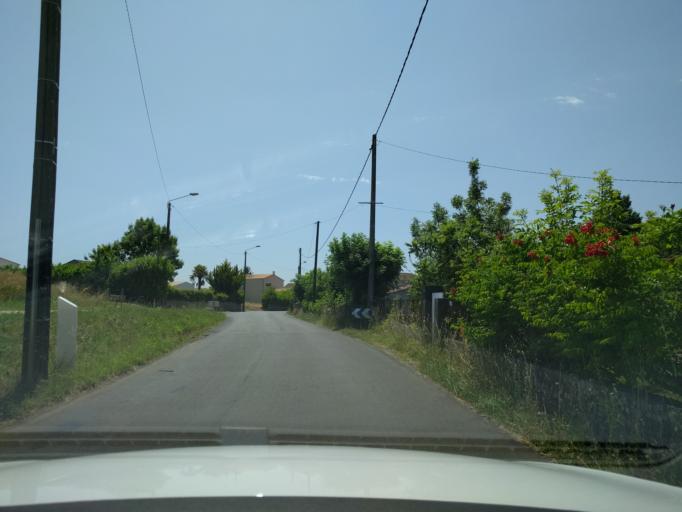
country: FR
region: Poitou-Charentes
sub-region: Departement des Deux-Sevres
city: Niort
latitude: 46.3521
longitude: -0.4536
